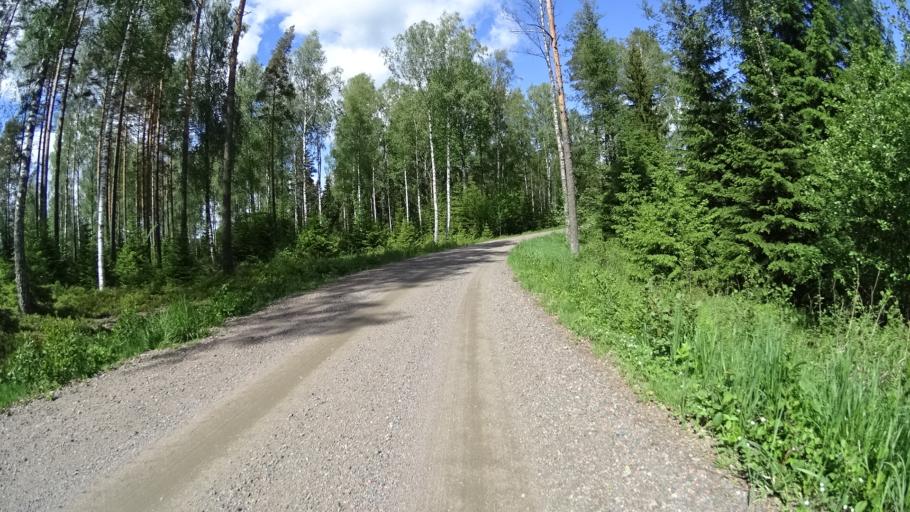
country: FI
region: Uusimaa
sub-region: Raaseporin
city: Karis
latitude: 60.1348
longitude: 23.6217
